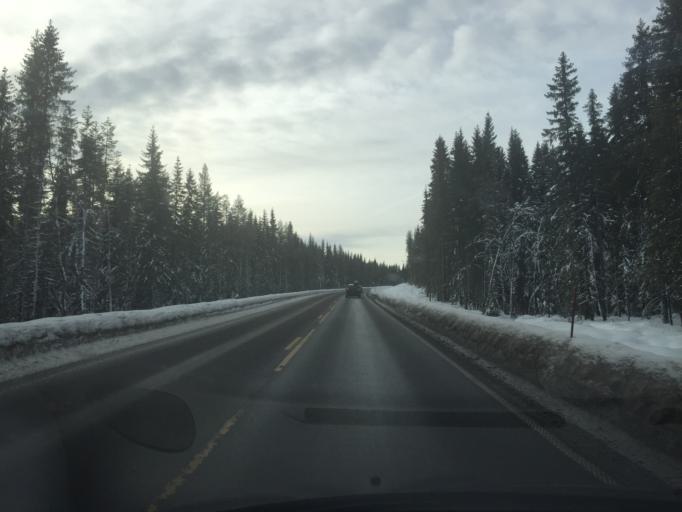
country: NO
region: Hedmark
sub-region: Trysil
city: Innbygda
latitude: 61.2514
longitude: 12.2982
